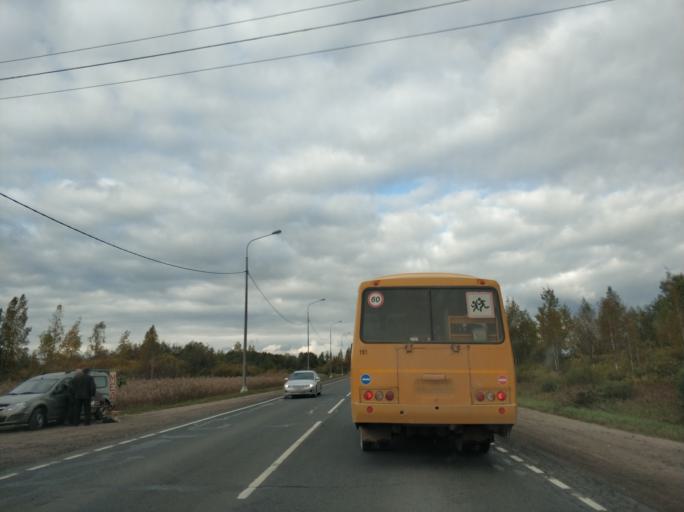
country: RU
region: Pskov
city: Ostrov
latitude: 57.3219
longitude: 28.3641
